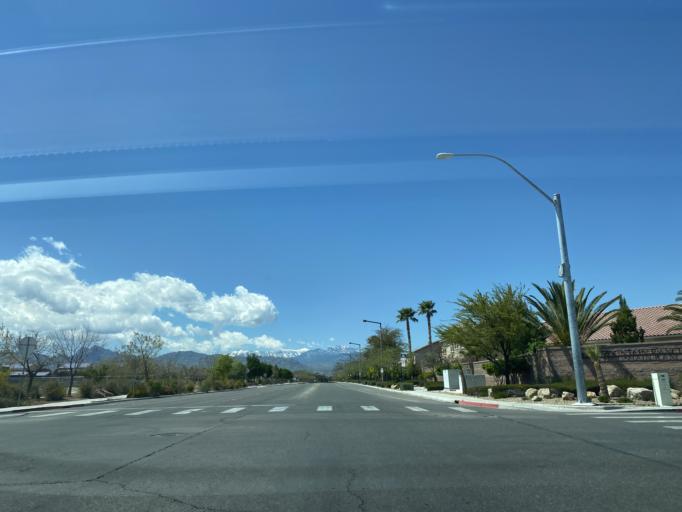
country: US
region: Nevada
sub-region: Clark County
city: North Las Vegas
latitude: 36.3130
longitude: -115.2155
